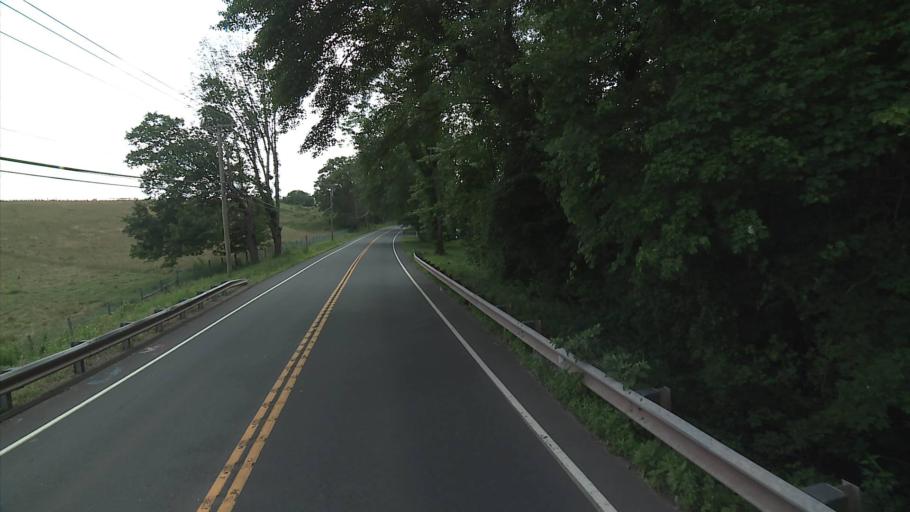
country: US
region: Connecticut
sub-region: Middlesex County
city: Portland
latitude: 41.5801
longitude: -72.6087
